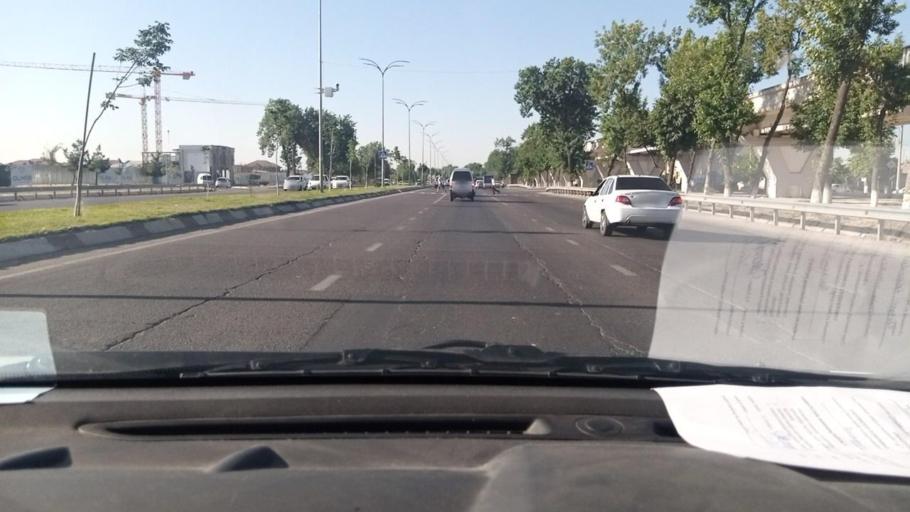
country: UZ
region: Toshkent Shahri
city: Bektemir
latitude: 41.2773
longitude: 69.3614
